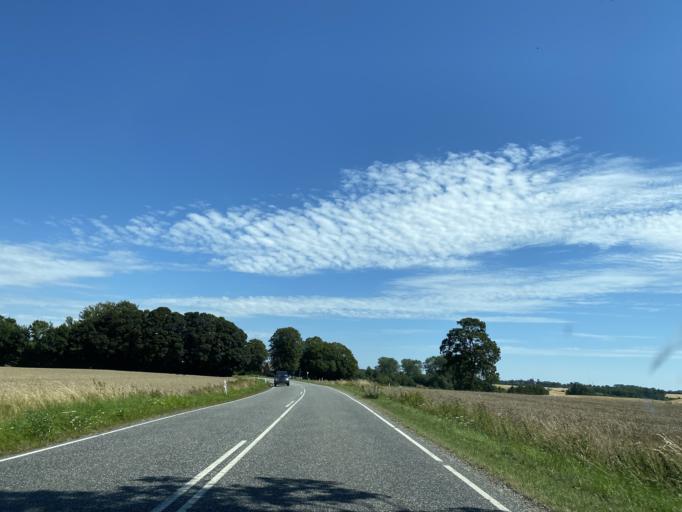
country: DK
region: South Denmark
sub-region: Nyborg Kommune
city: Ullerslev
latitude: 55.2522
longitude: 10.6437
